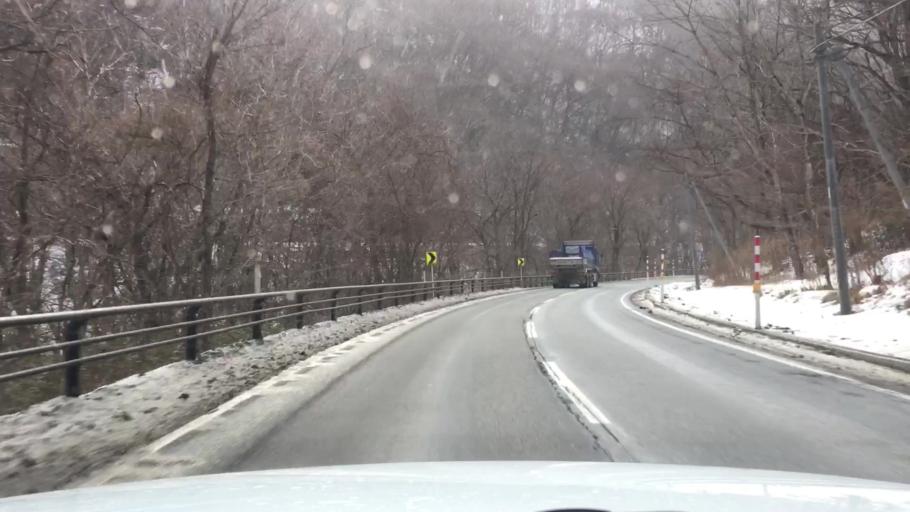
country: JP
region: Iwate
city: Tono
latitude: 39.6170
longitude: 141.5027
